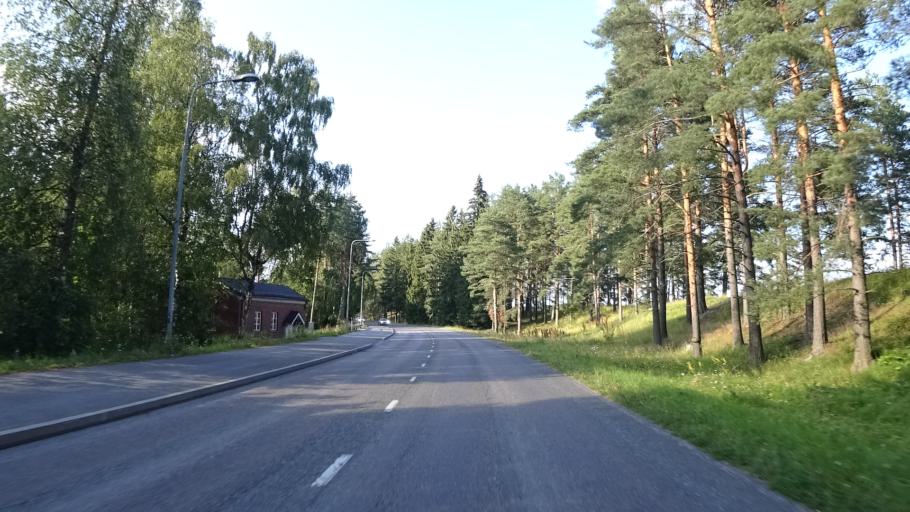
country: FI
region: South Karelia
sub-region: Imatra
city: Imatra
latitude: 61.1792
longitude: 28.7816
